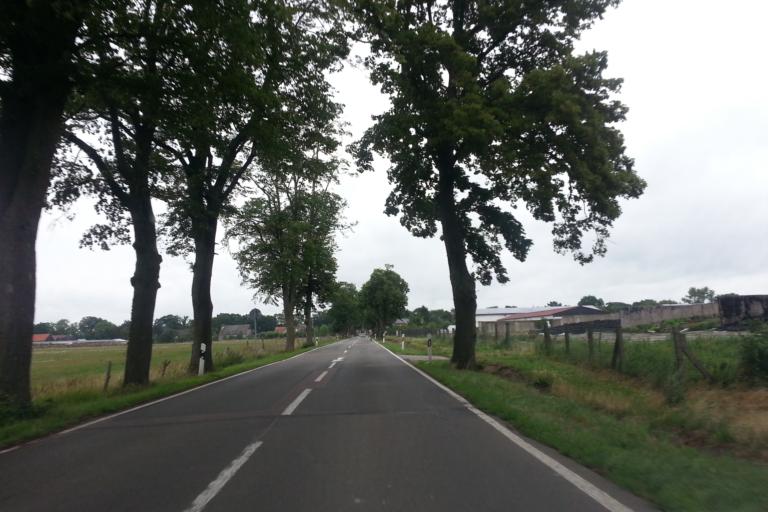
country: DE
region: Mecklenburg-Vorpommern
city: Ferdinandshof
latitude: 53.6779
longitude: 13.9153
